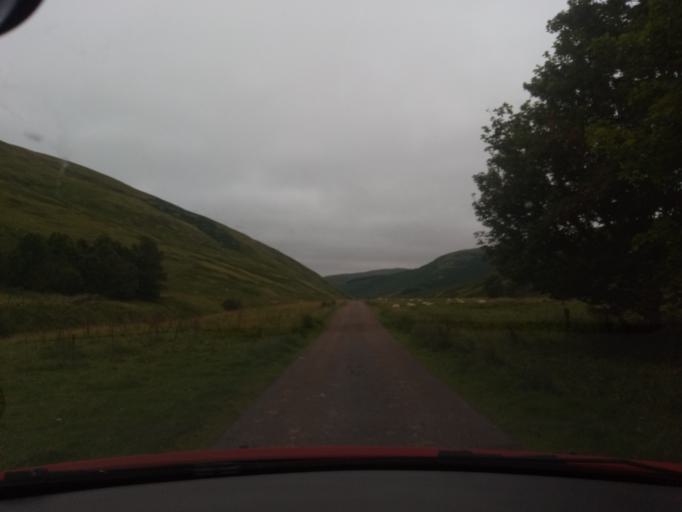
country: GB
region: England
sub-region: Northumberland
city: Rochester
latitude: 55.3862
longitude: -2.2125
